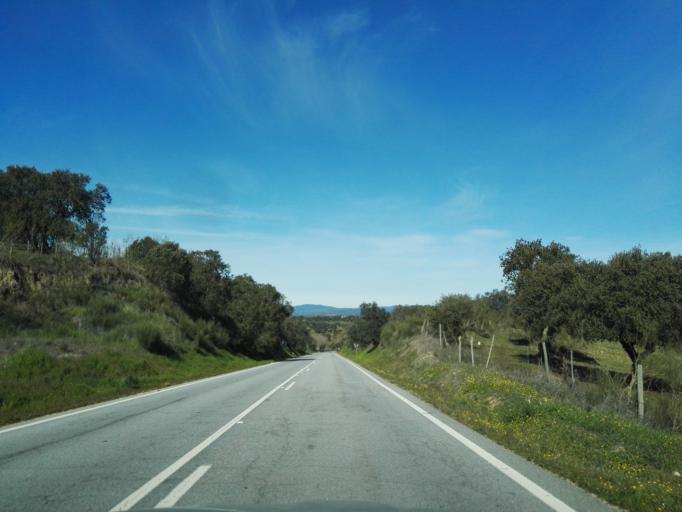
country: PT
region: Portalegre
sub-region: Arronches
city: Arronches
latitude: 39.0860
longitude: -7.2825
